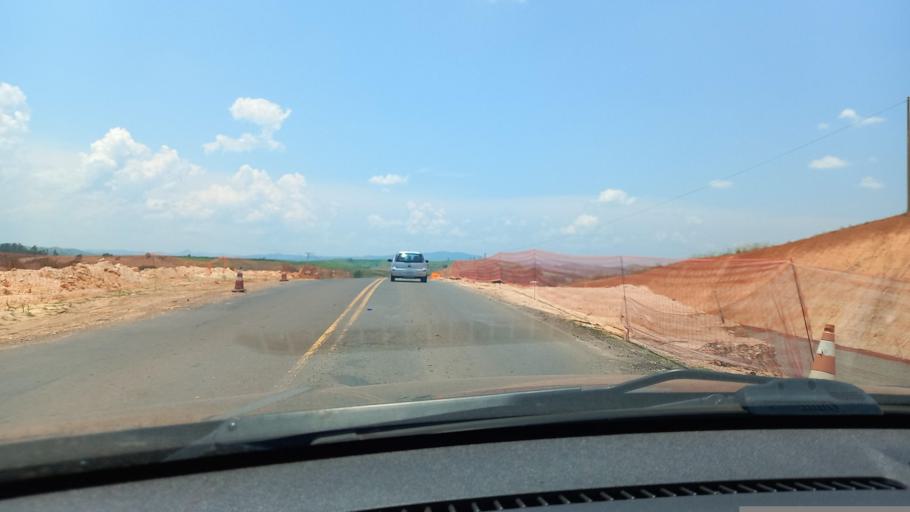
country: BR
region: Sao Paulo
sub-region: Itapira
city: Itapira
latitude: -22.3984
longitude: -46.8529
